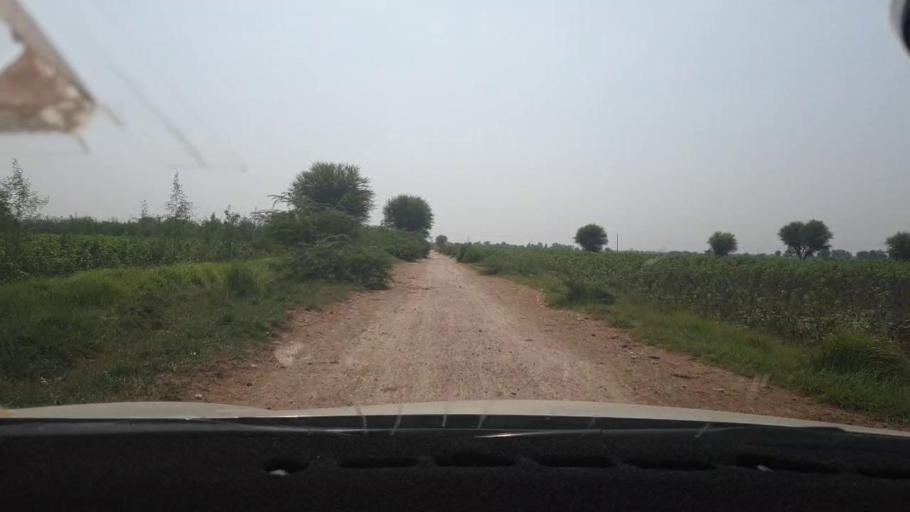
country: PK
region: Sindh
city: Tando Mittha Khan
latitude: 25.9332
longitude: 69.2247
